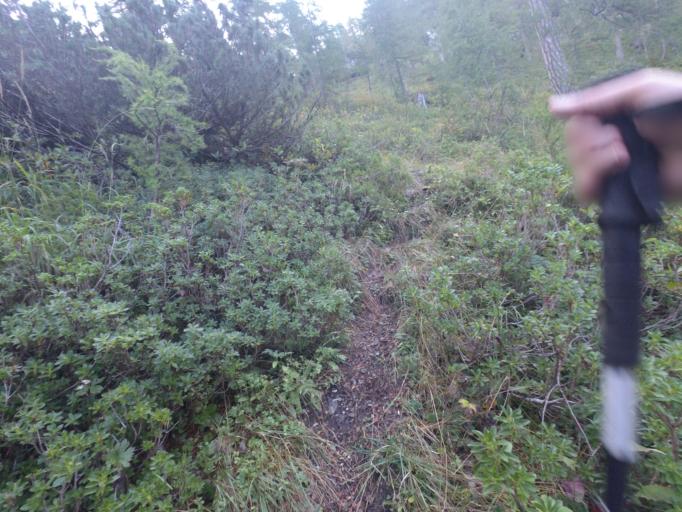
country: AT
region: Salzburg
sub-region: Politischer Bezirk Sankt Johann im Pongau
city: Untertauern
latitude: 47.2303
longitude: 13.4241
